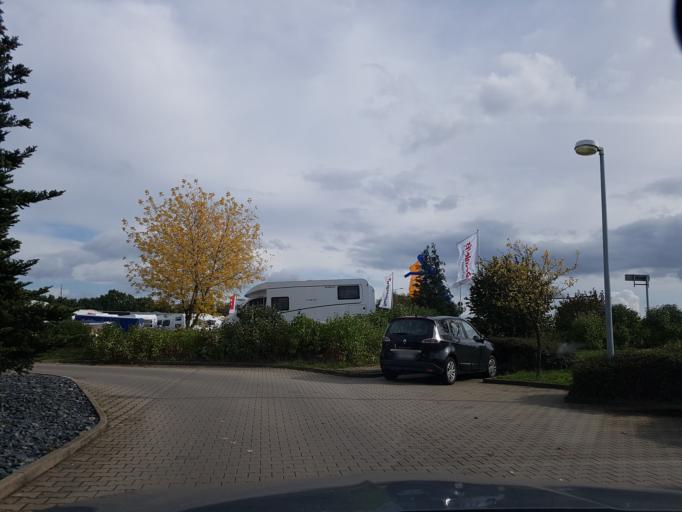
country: DE
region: Saxony
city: Riesa
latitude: 51.2949
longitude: 13.2862
